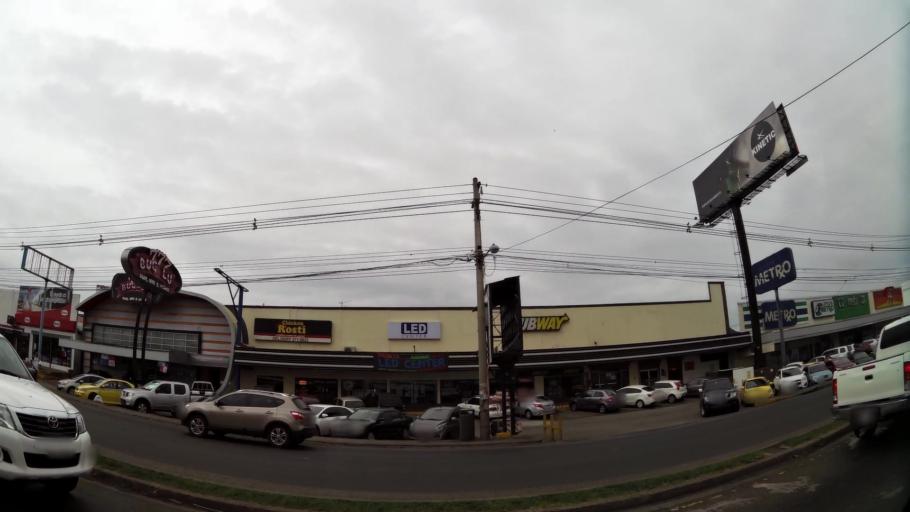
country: PA
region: Panama
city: Panama
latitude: 8.9989
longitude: -79.5256
